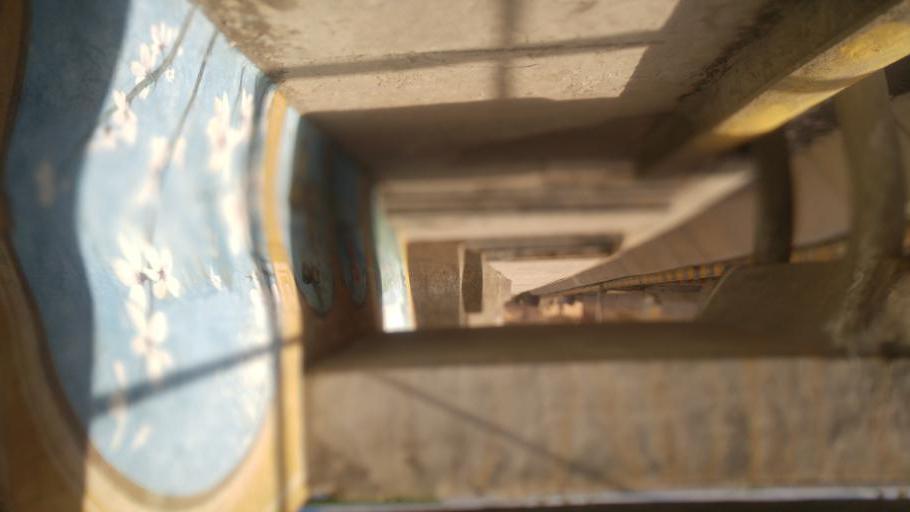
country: IR
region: Markazi
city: Shazand
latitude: 34.0453
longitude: 49.4181
